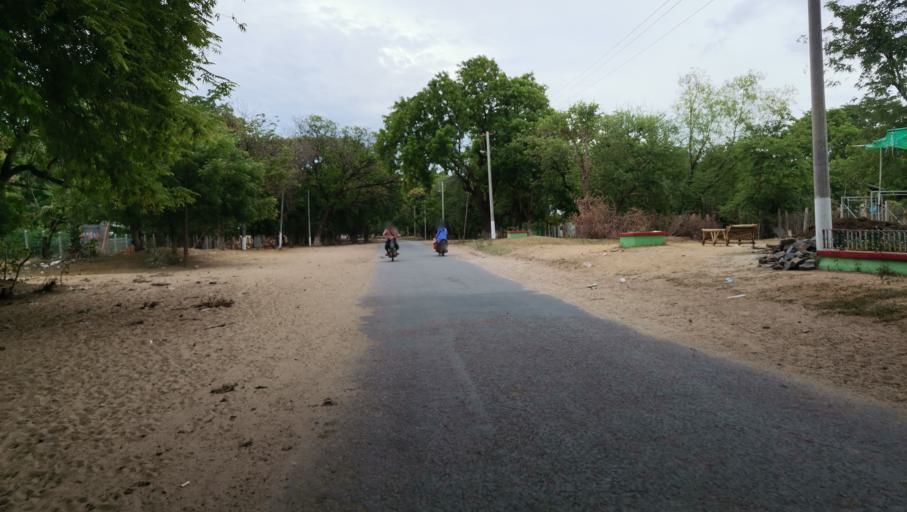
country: MM
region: Mandalay
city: Myingyan
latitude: 21.8451
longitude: 95.4282
